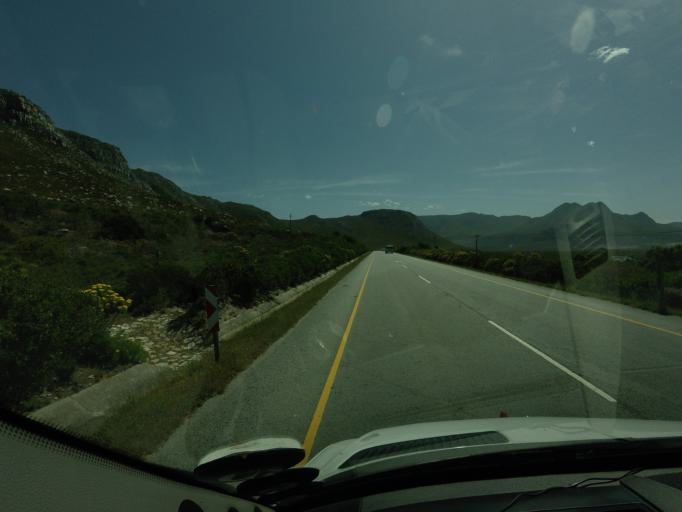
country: ZA
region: Western Cape
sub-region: Overberg District Municipality
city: Grabouw
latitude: -34.3552
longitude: 18.9732
